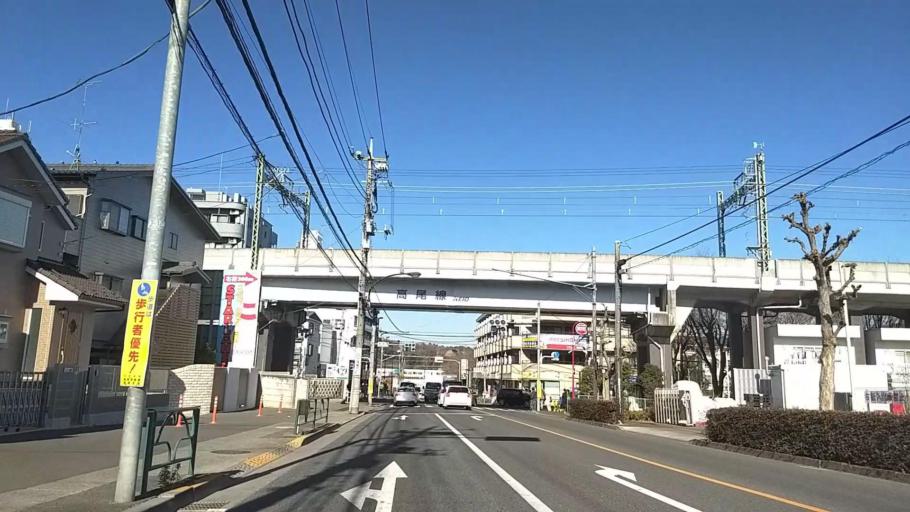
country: JP
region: Tokyo
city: Hachioji
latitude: 35.6411
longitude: 139.2865
